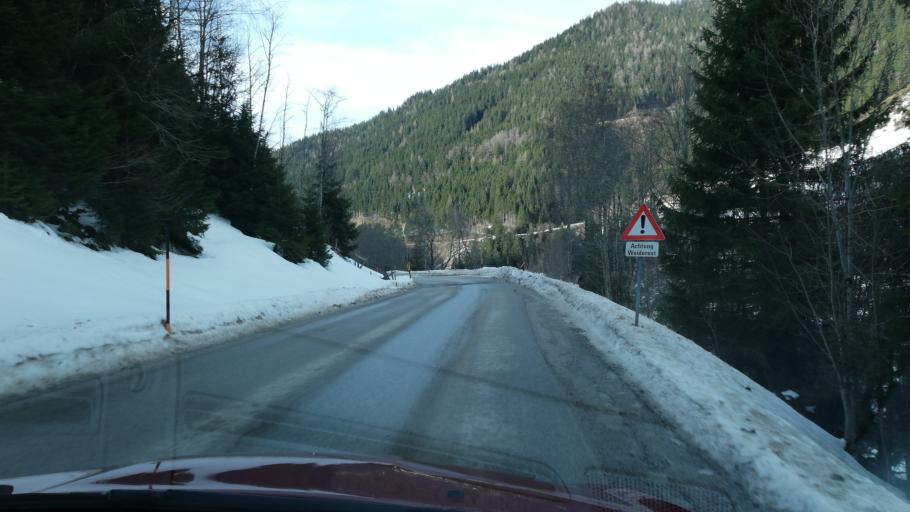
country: AT
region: Styria
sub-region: Politischer Bezirk Liezen
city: Donnersbach
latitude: 47.4296
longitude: 14.1607
